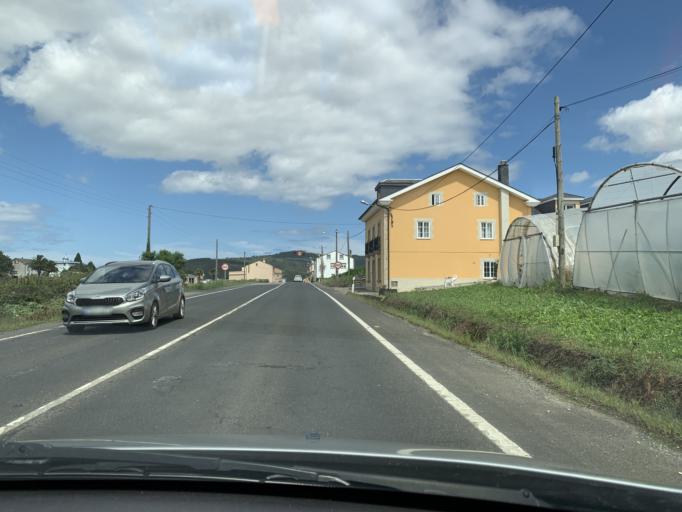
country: ES
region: Galicia
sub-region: Provincia de Lugo
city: Barreiros
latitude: 43.4943
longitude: -7.2752
